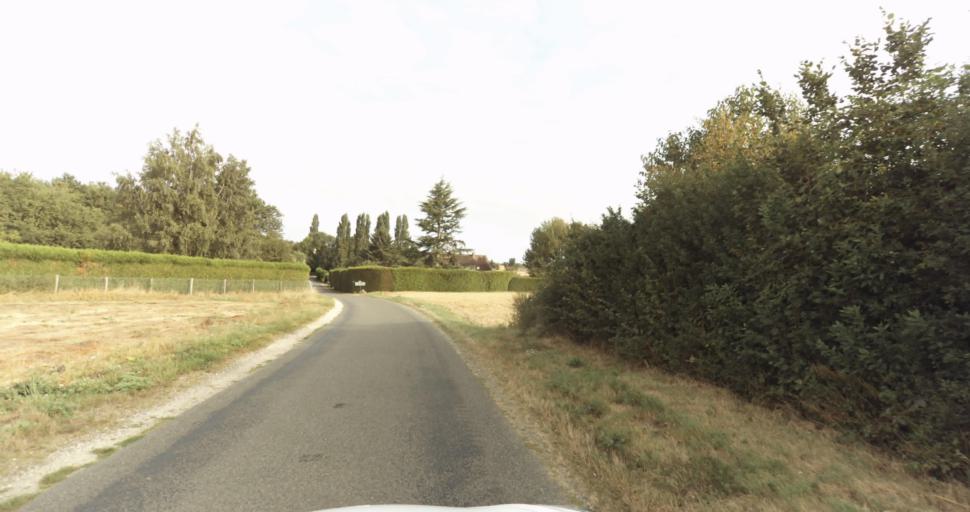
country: FR
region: Centre
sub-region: Departement d'Eure-et-Loir
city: Saint-Remy-sur-Avre
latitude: 48.8126
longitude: 1.2426
